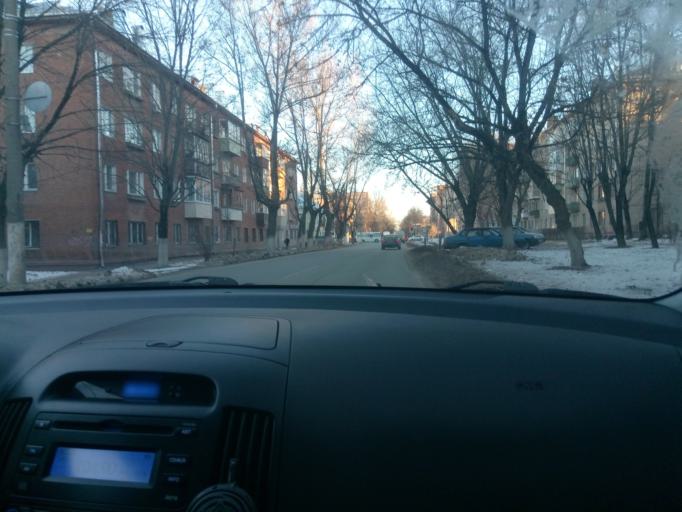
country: RU
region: Tula
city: Mendeleyevskiy
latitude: 54.1654
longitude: 37.5788
